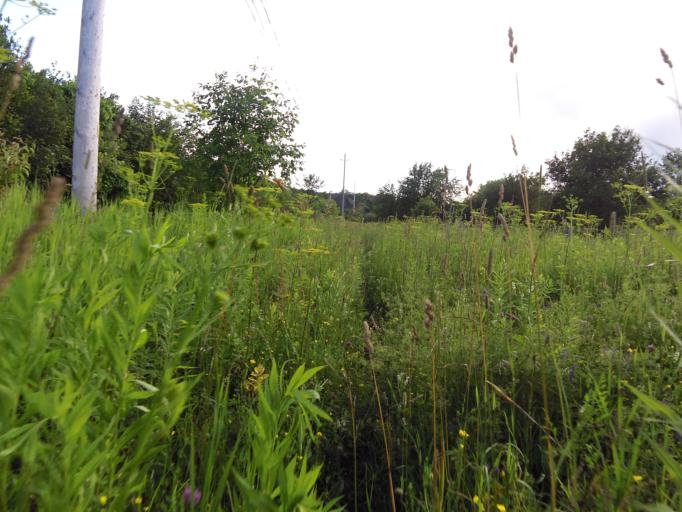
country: CA
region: Ontario
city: Bells Corners
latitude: 45.3415
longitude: -75.8636
